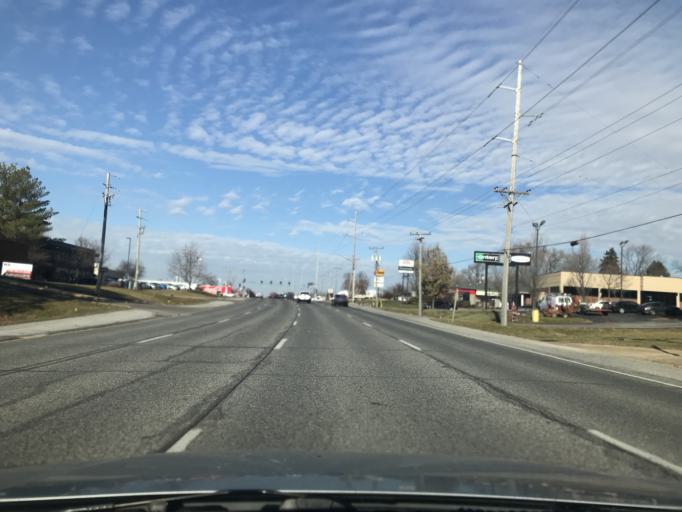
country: US
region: Iowa
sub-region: Scott County
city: Davenport
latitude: 41.5659
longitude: -90.5676
